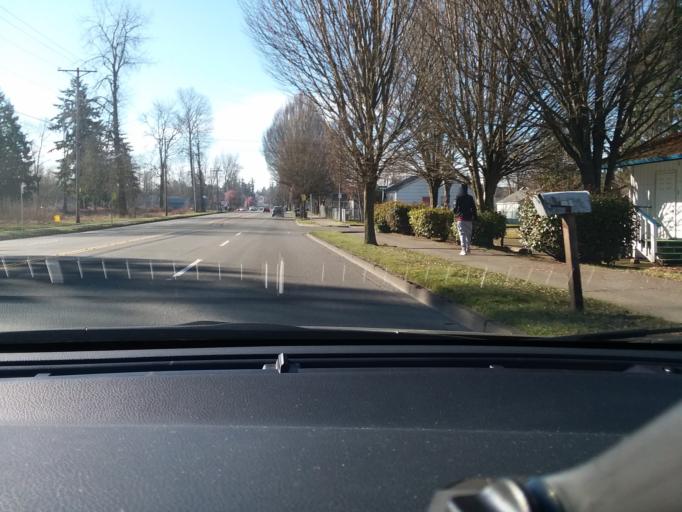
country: US
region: Washington
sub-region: Pierce County
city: Waller
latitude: 47.2085
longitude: -122.4080
